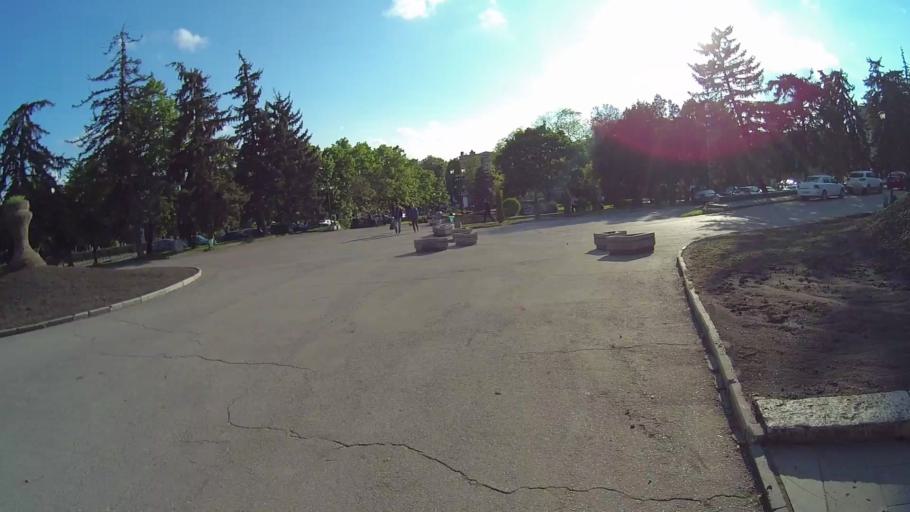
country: RU
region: Stavropol'skiy
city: Goryachevodskiy
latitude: 44.0371
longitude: 43.0770
